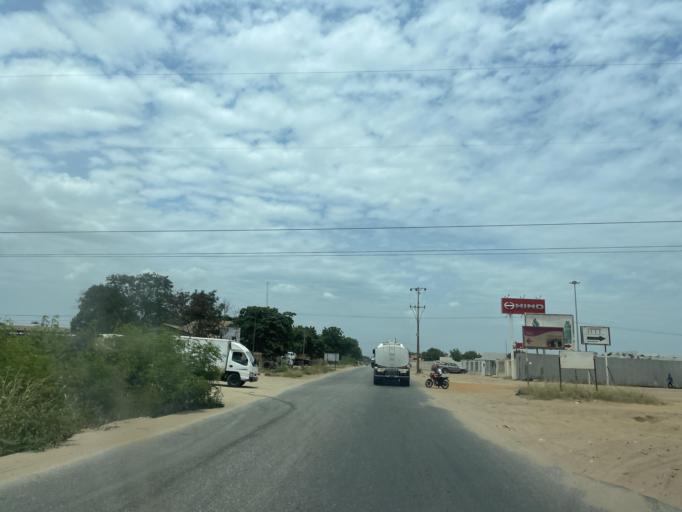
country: AO
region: Luanda
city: Luanda
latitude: -8.9287
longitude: 13.3954
